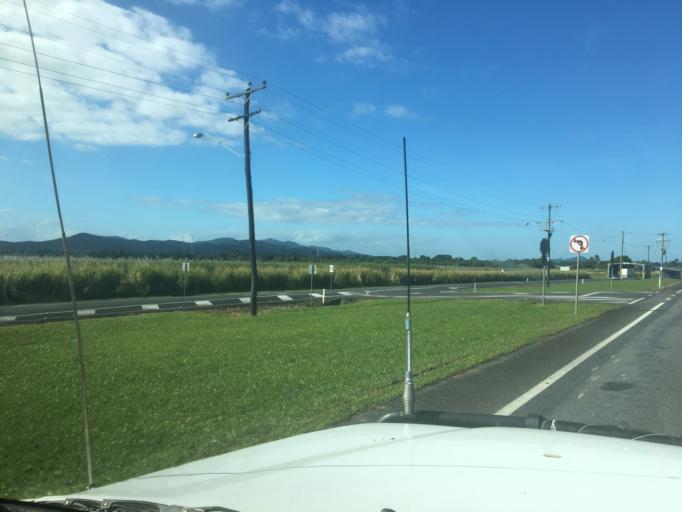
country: AU
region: Queensland
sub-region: Cassowary Coast
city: Innisfail
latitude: -17.3197
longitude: 145.9279
